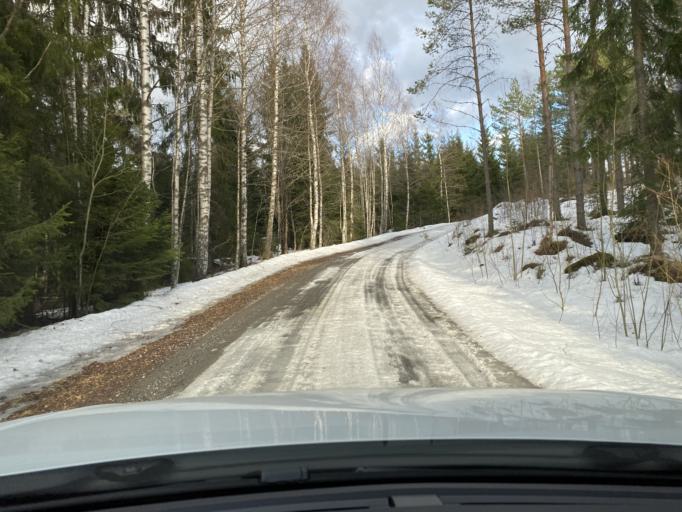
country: FI
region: Pirkanmaa
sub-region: Lounais-Pirkanmaa
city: Mouhijaervi
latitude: 61.4348
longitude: 22.9794
